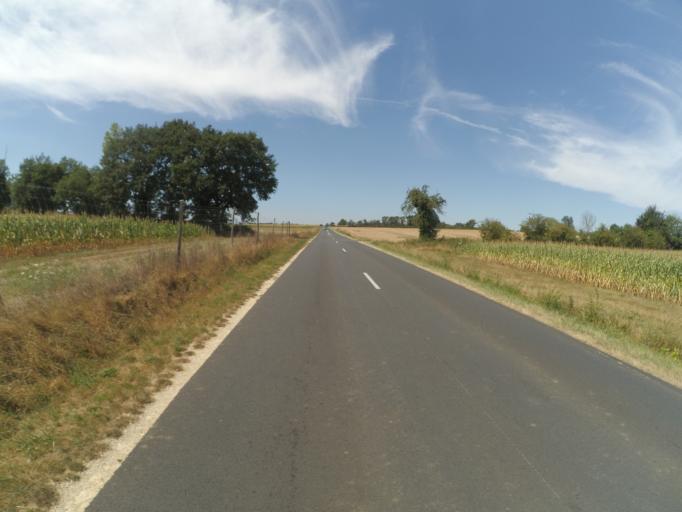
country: FR
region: Poitou-Charentes
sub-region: Departement de la Vienne
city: Saint-Maurice-la-Clouere
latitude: 46.3616
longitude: 0.4332
